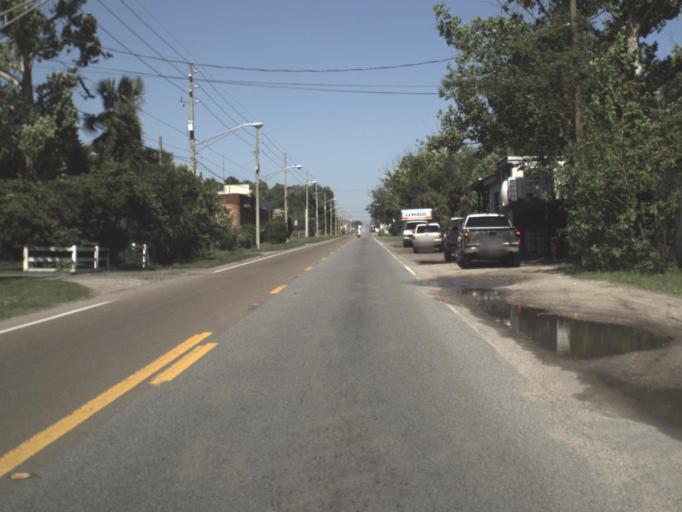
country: US
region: Florida
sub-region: Duval County
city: Jacksonville
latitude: 30.3257
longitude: -81.7416
